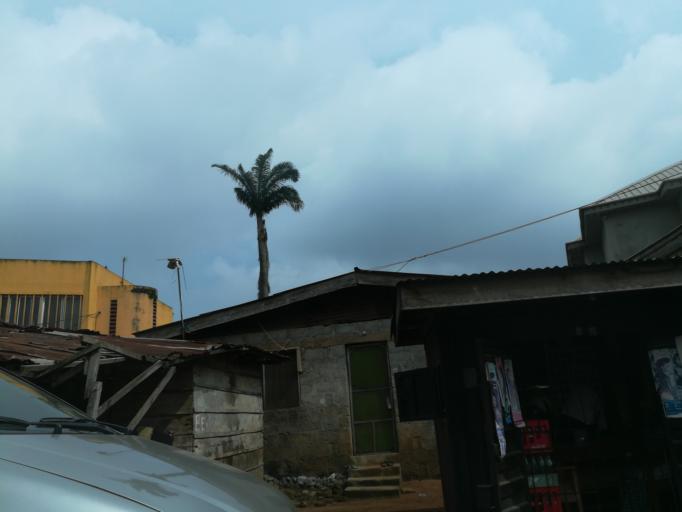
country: NG
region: Lagos
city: Agege
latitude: 6.5913
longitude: 3.3038
